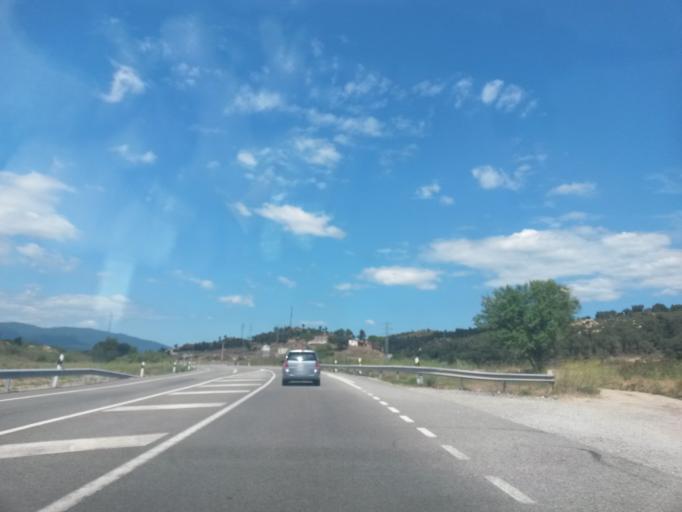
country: ES
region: Catalonia
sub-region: Provincia de Girona
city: Biure
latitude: 42.3549
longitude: 2.9047
